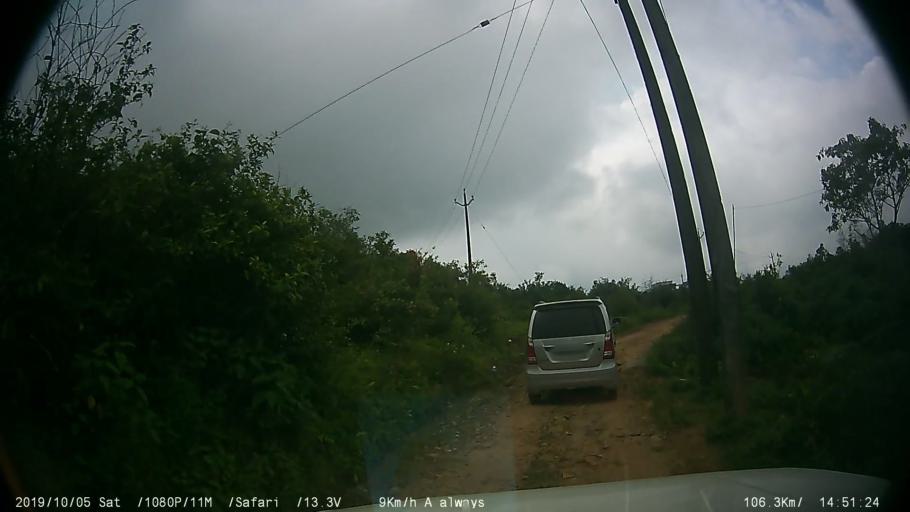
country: IN
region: Kerala
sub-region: Kottayam
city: Erattupetta
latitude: 9.6187
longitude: 76.9366
